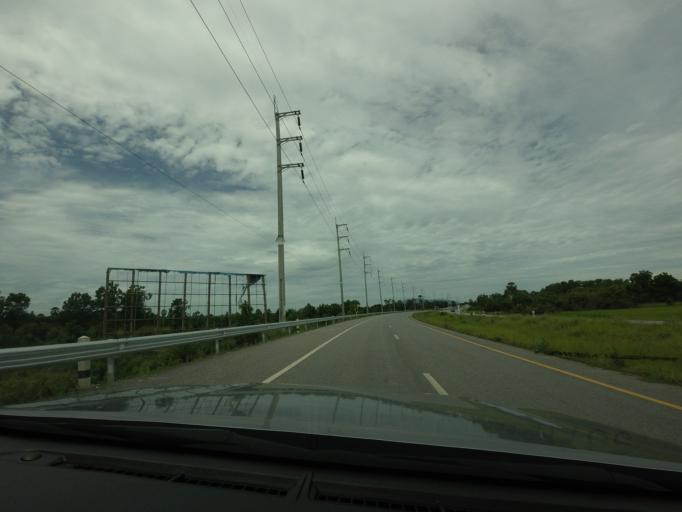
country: TH
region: Pattani
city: Pattani
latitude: 6.8400
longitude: 101.2251
